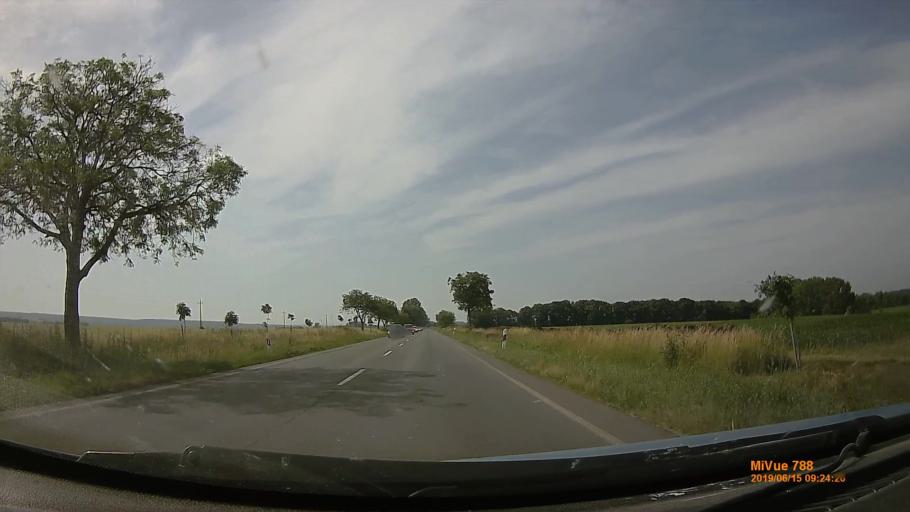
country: HU
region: Tolna
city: Tamasi
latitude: 46.5517
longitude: 18.1677
